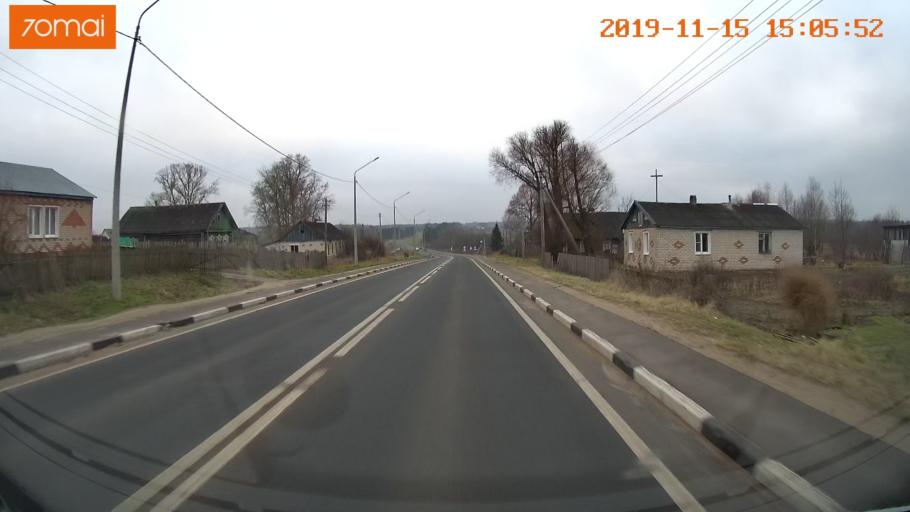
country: RU
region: Jaroslavl
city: Prechistoye
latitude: 58.3988
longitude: 40.3183
